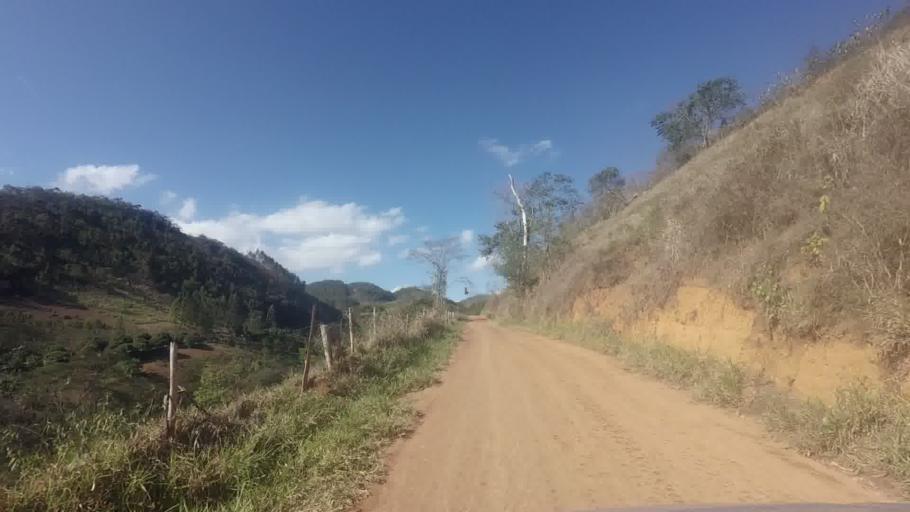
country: BR
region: Espirito Santo
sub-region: Sao Jose Do Calcado
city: Sao Jose do Calcado
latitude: -21.0300
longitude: -41.5839
